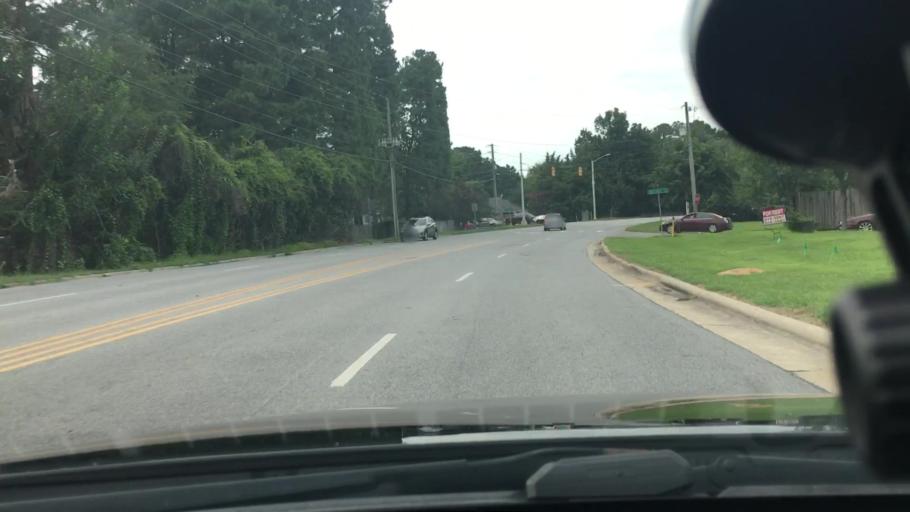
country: US
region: North Carolina
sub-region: Pitt County
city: Greenville
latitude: 35.5856
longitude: -77.3465
